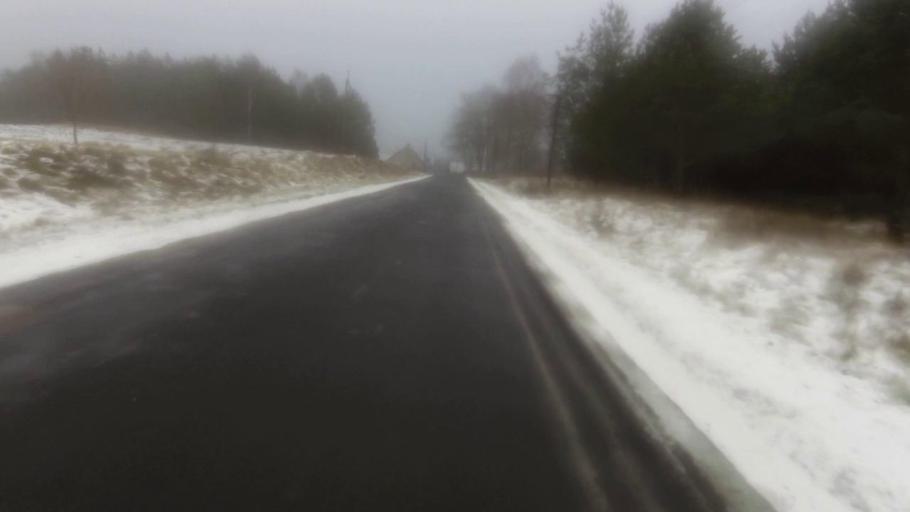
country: PL
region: West Pomeranian Voivodeship
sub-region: Powiat drawski
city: Wierzchowo
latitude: 53.4444
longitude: 16.1601
